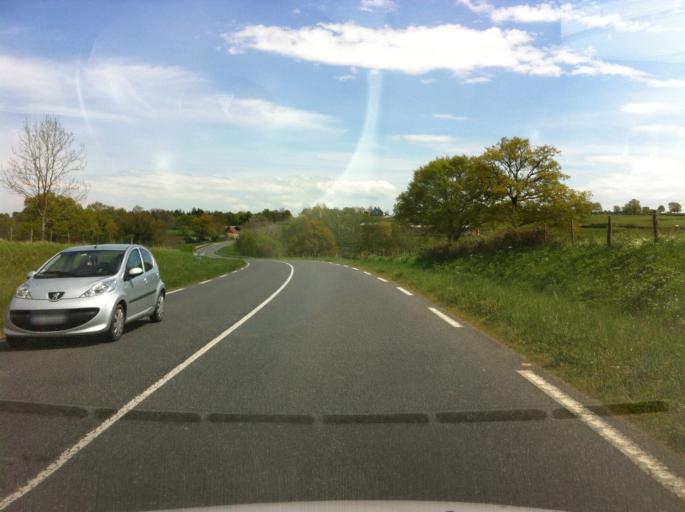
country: FR
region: Auvergne
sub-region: Departement de l'Allier
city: Chantelle
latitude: 46.3188
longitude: 3.1088
